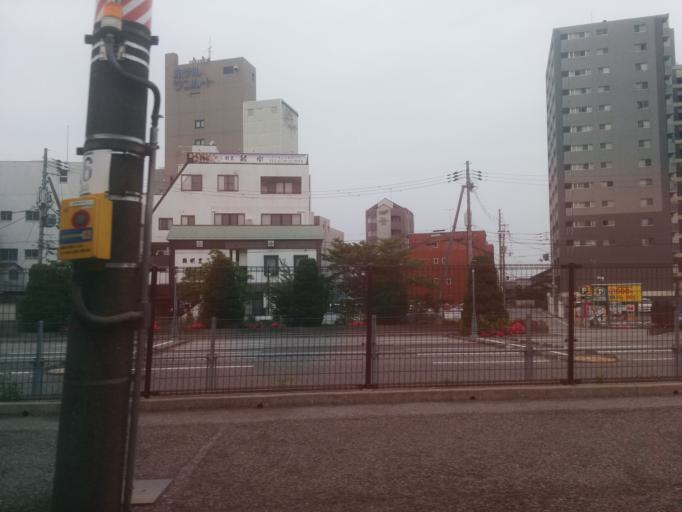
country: JP
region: Shiga Prefecture
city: Hikone
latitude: 35.2729
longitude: 136.2634
